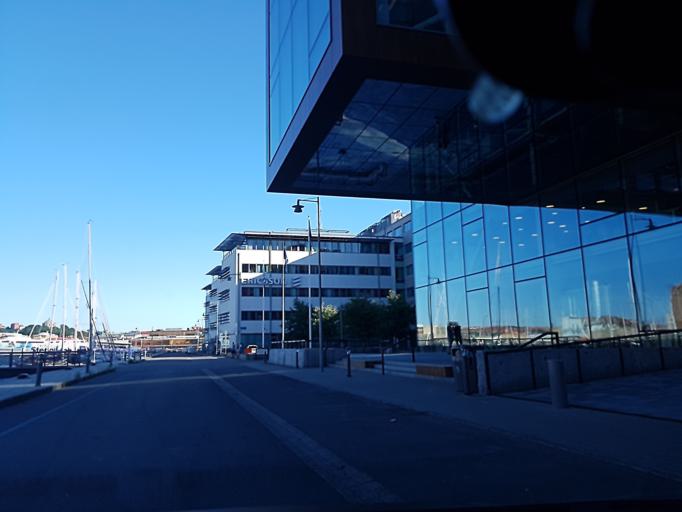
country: SE
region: Vaestra Goetaland
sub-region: Goteborg
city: Goeteborg
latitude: 57.7066
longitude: 11.9415
